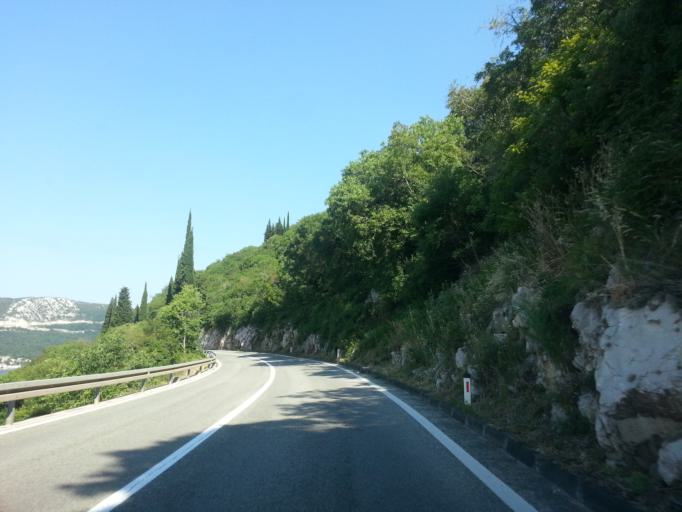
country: HR
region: Primorsko-Goranska
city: Krasica
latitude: 45.2987
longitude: 14.5593
